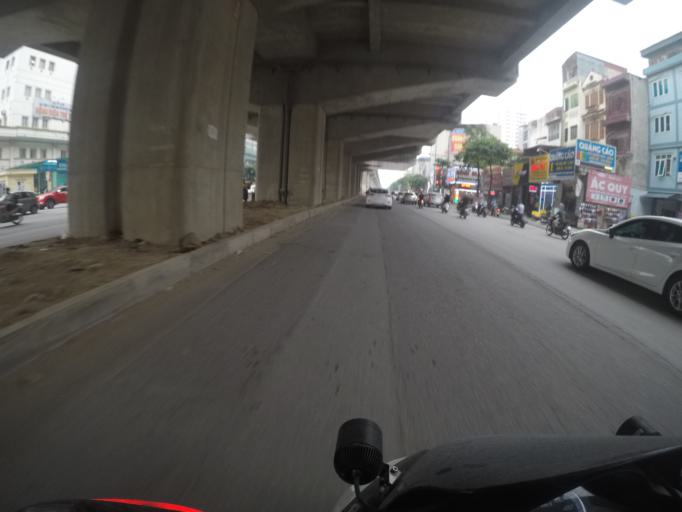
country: VN
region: Ha Noi
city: Thanh Xuan
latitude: 20.9841
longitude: 105.7929
